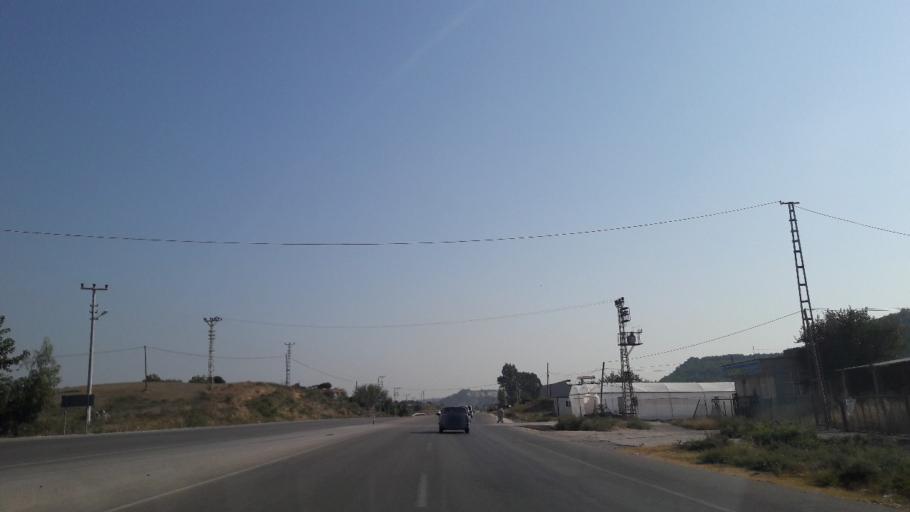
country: TR
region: Adana
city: Yuregir
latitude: 37.0657
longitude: 35.4487
